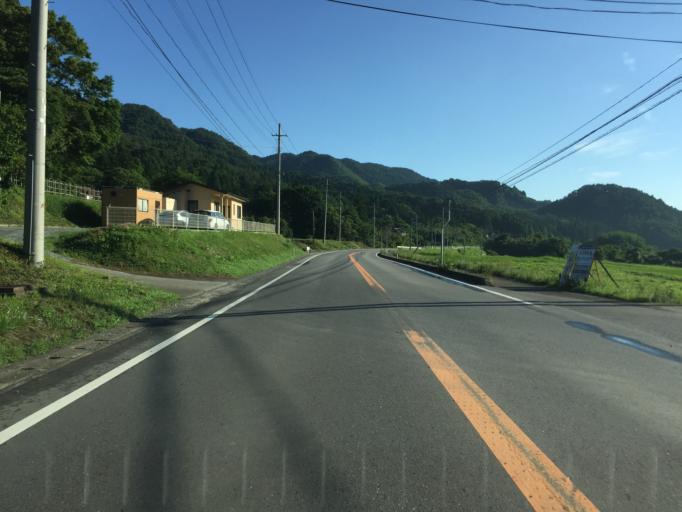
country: JP
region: Miyagi
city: Marumori
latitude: 37.7682
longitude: 140.8601
